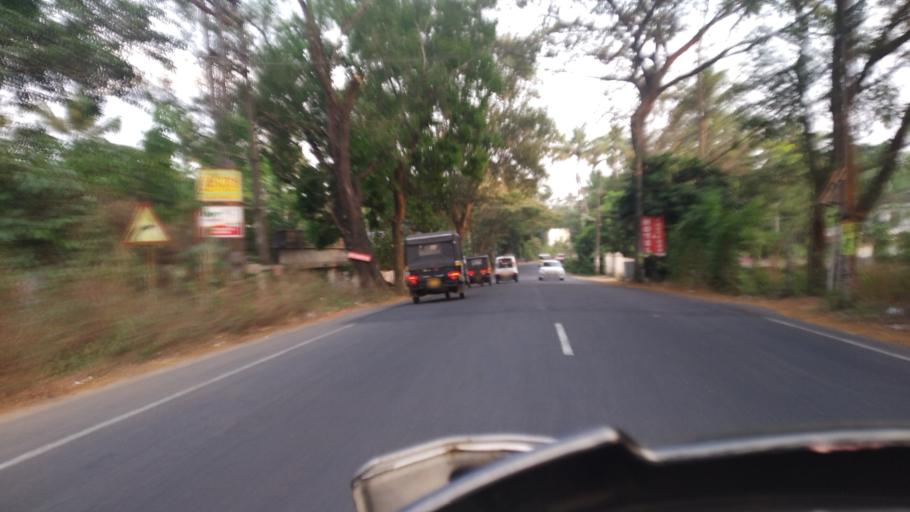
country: IN
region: Kerala
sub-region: Thrissur District
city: Kodungallur
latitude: 10.2530
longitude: 76.1859
